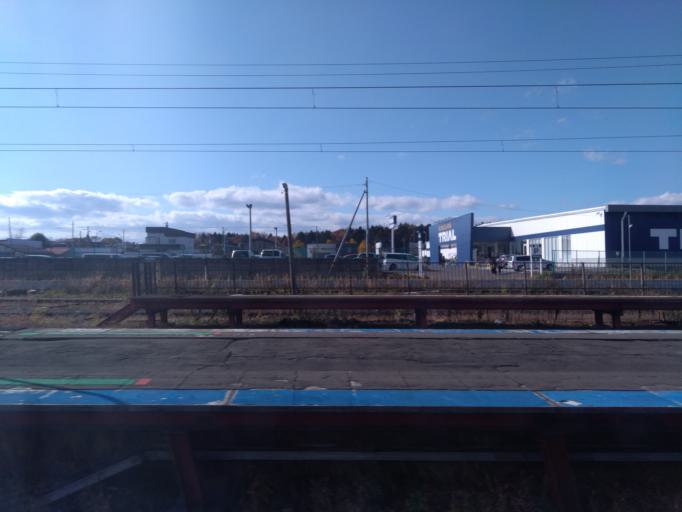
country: JP
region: Hokkaido
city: Kitahiroshima
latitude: 42.9210
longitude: 141.5733
